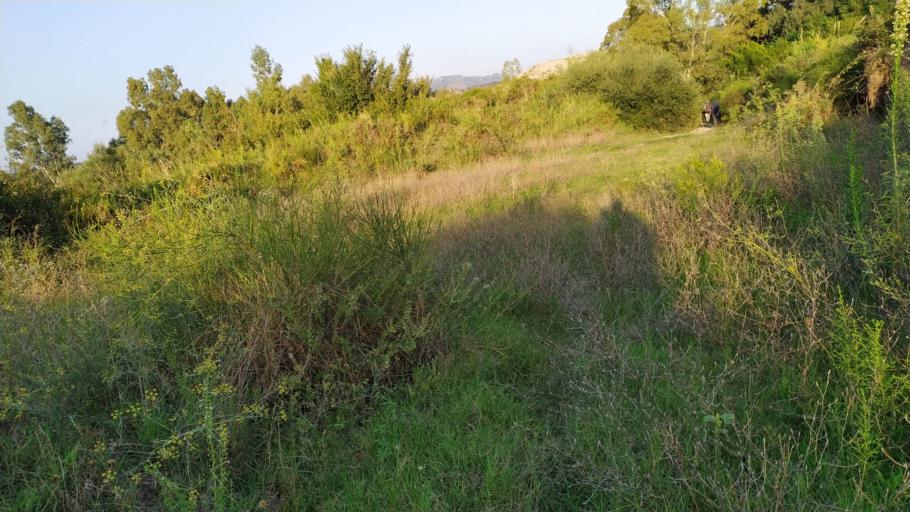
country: IT
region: Sicily
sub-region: Messina
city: Saponara Marittima
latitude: 38.2253
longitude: 15.4349
